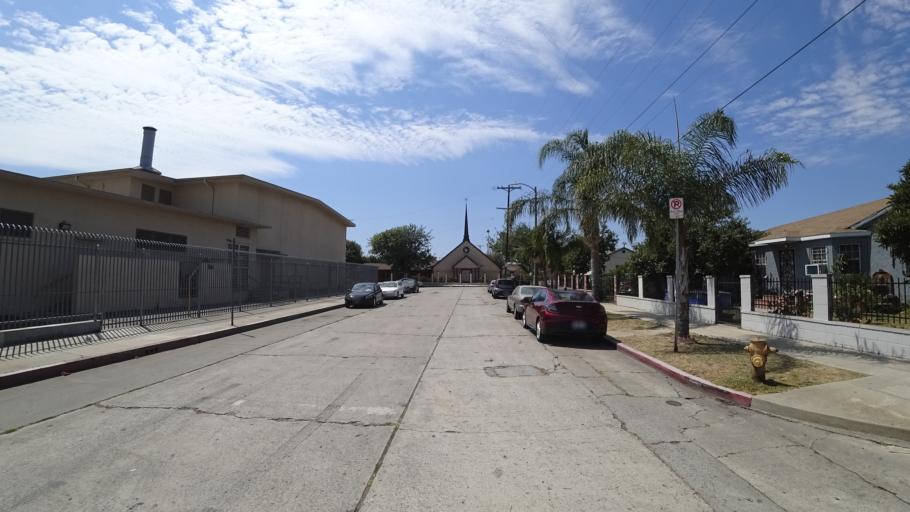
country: US
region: California
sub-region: Los Angeles County
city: Westmont
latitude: 33.9519
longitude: -118.2894
